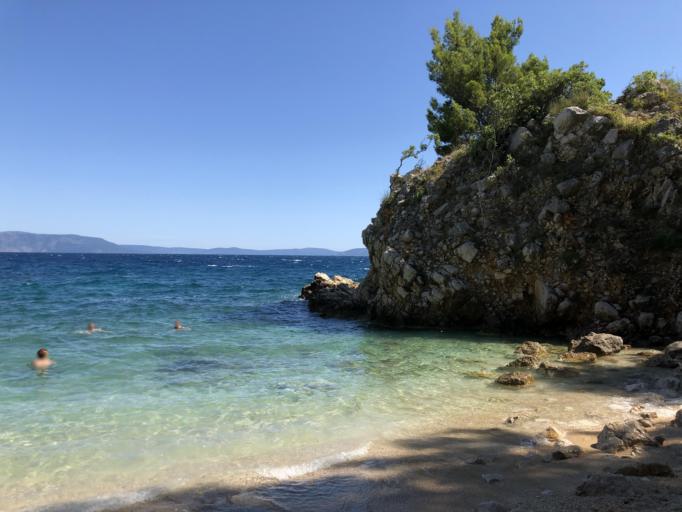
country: HR
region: Istarska
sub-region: Grad Labin
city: Rabac
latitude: 45.0877
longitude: 14.1815
